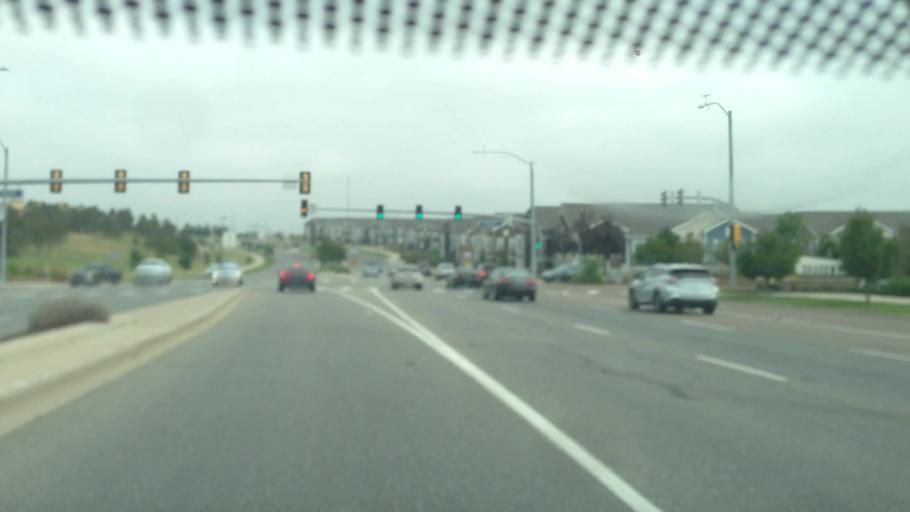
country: US
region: Colorado
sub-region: Douglas County
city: Parker
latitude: 39.6039
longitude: -104.7030
